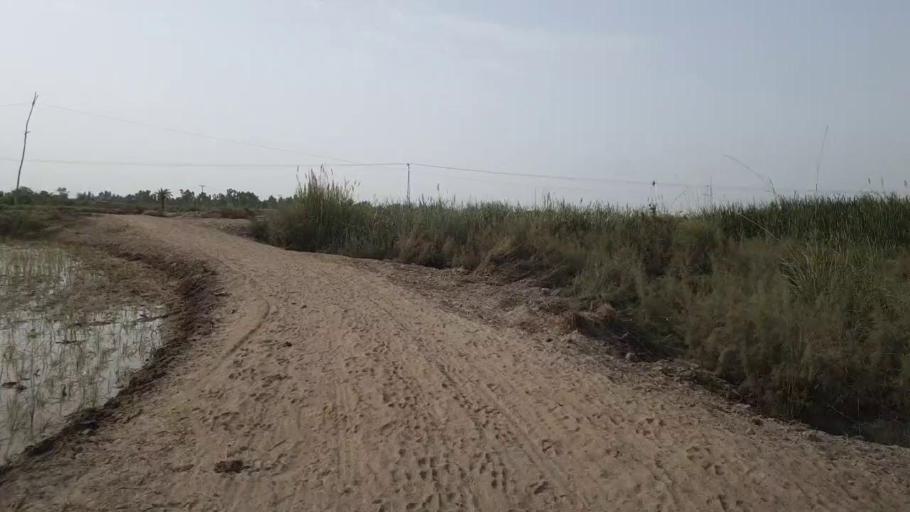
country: PK
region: Sindh
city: Daur
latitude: 26.4177
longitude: 68.1600
